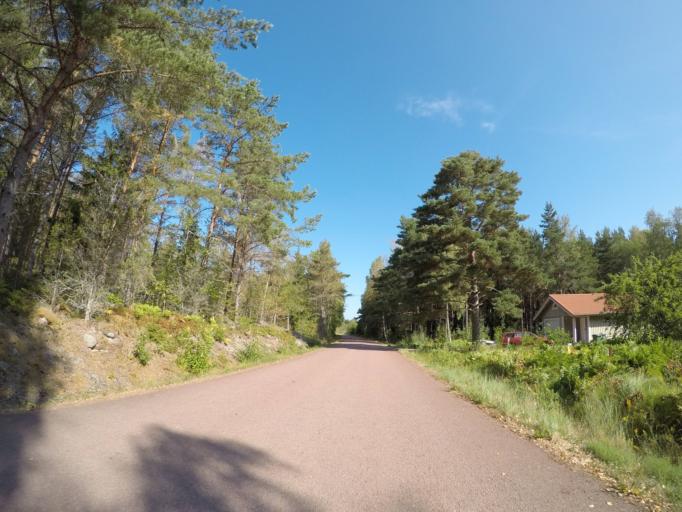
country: AX
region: Alands landsbygd
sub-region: Finstroem
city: Finstroem
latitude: 60.2759
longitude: 19.9181
